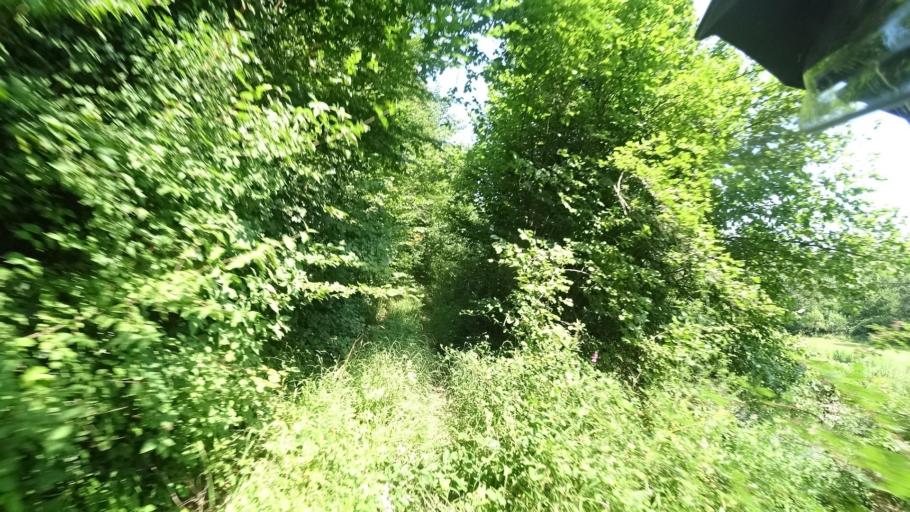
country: HR
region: Karlovacka
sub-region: Grad Ogulin
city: Ogulin
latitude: 45.3096
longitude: 15.1762
